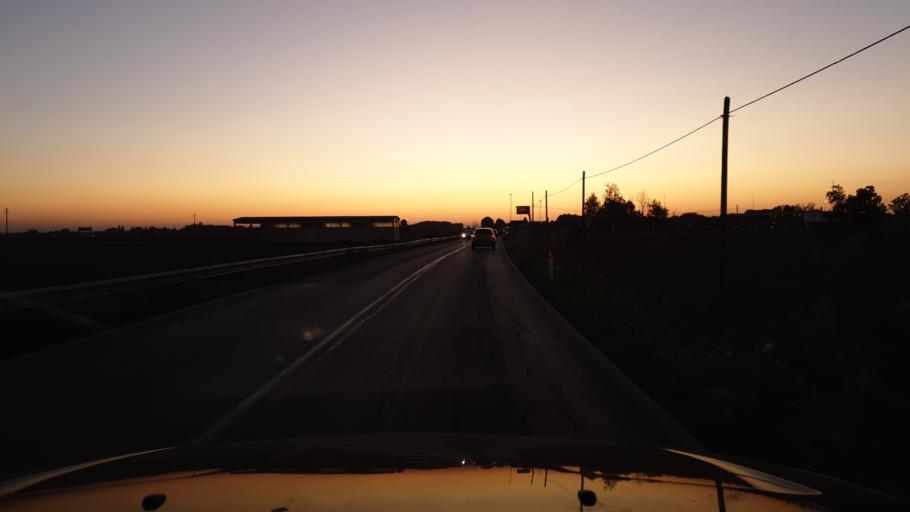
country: IT
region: Emilia-Romagna
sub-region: Provincia di Bologna
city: Altedo
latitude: 44.6844
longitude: 11.4847
